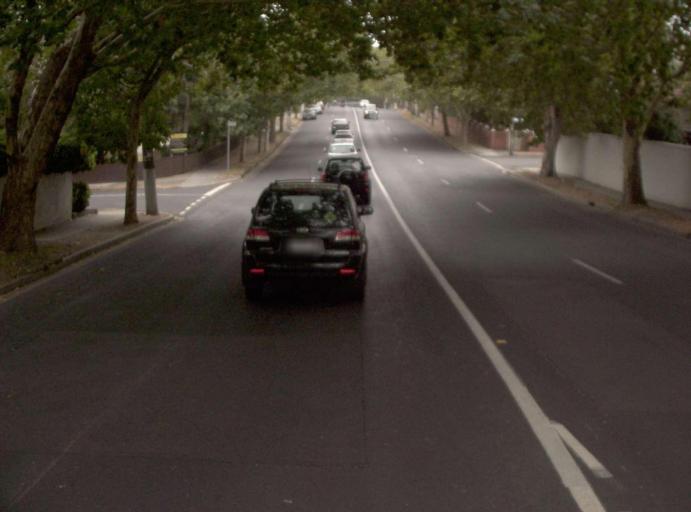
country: AU
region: Victoria
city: Toorak
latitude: -37.8487
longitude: 145.0124
